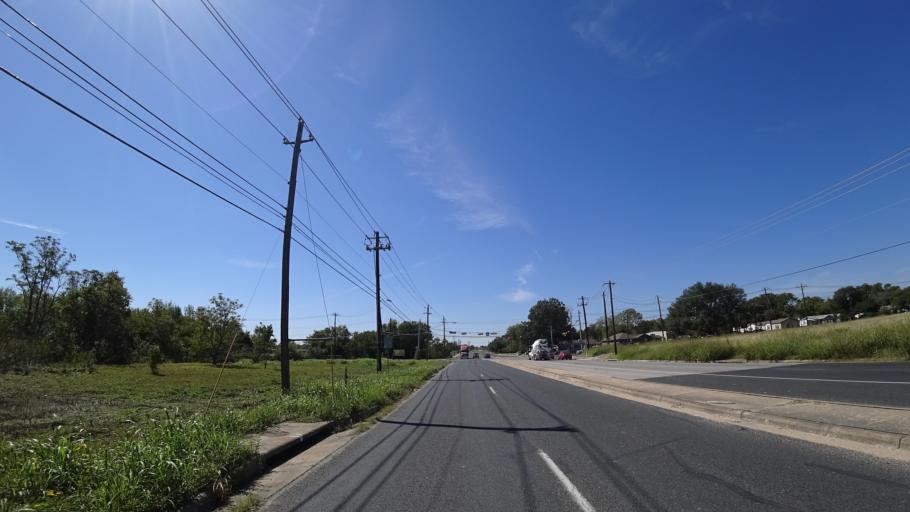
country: US
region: Texas
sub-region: Travis County
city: Austin
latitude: 30.1925
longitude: -97.6976
